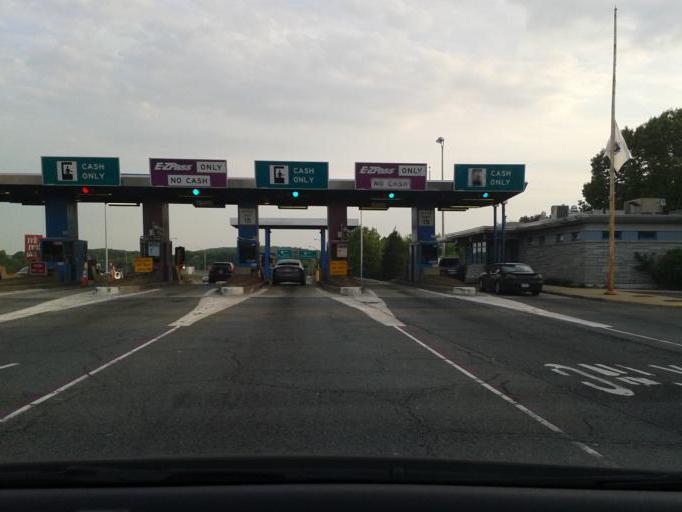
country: US
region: Massachusetts
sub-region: Middlesex County
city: Cochituate
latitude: 42.3104
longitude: -71.3865
